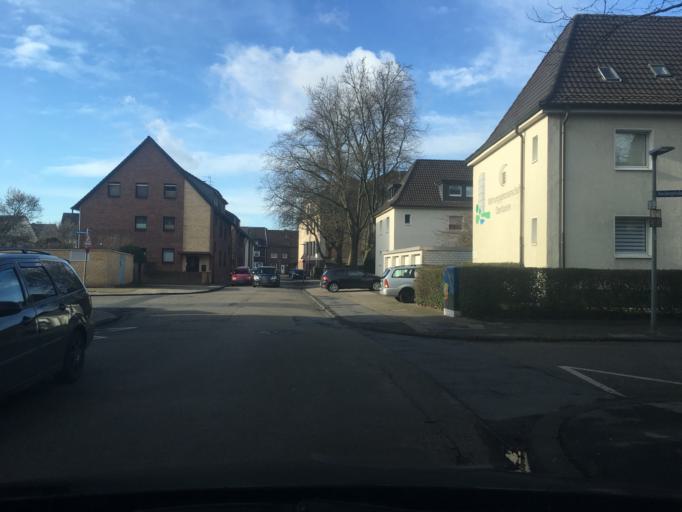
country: DE
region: North Rhine-Westphalia
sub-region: Regierungsbezirk Dusseldorf
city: Oberhausen
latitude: 51.4730
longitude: 6.8807
